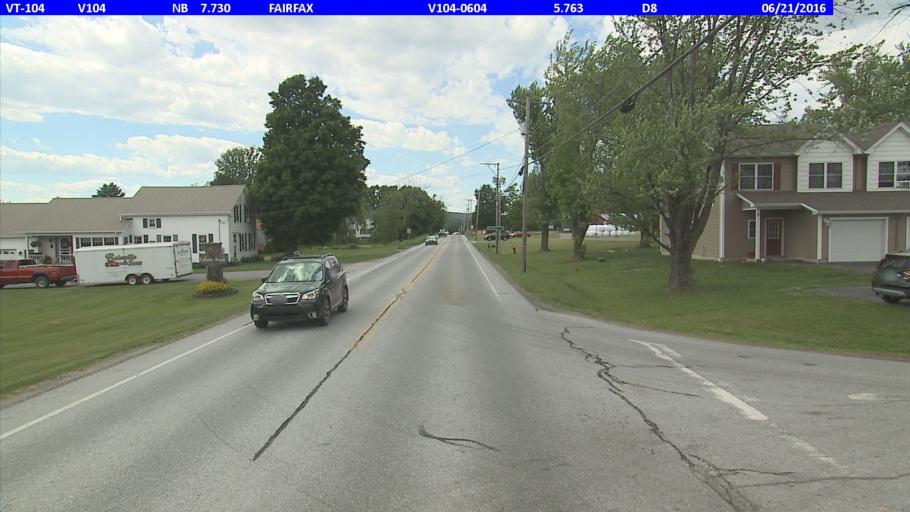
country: US
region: Vermont
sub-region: Chittenden County
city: Milton
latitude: 44.6716
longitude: -73.0162
